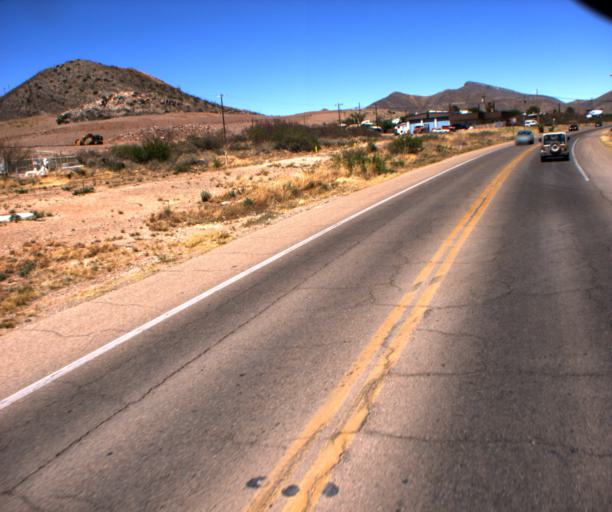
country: US
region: Arizona
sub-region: Cochise County
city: Bisbee
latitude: 31.4147
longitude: -109.8995
